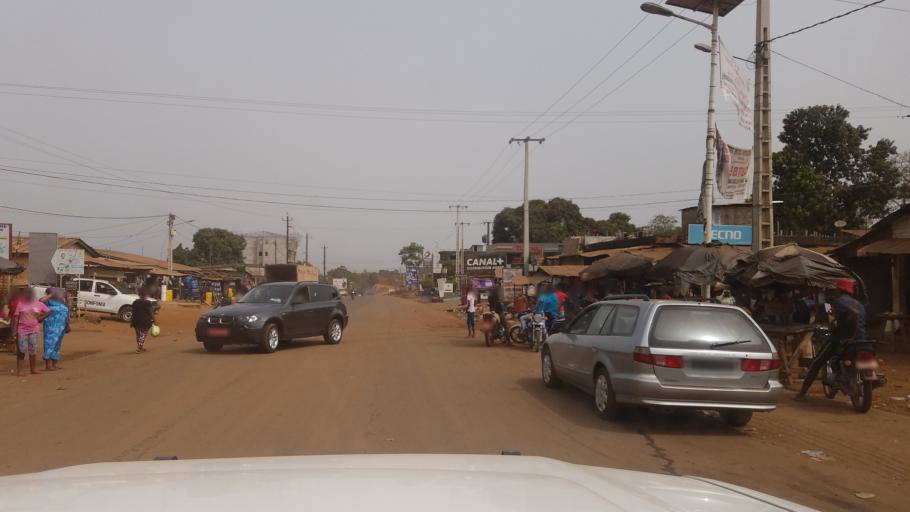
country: GN
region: Kindia
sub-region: Prefecture de Dubreka
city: Dubreka
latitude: 9.6710
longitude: -13.5839
